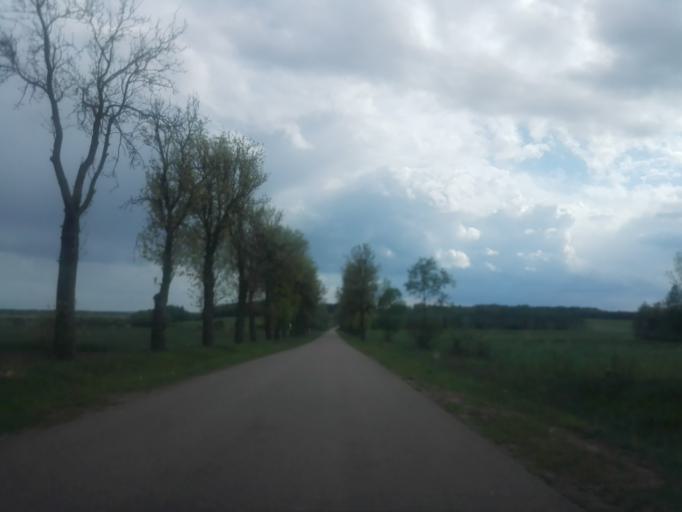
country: PL
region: Podlasie
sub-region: Powiat lomzynski
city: Wizna
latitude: 53.2746
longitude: 22.4536
